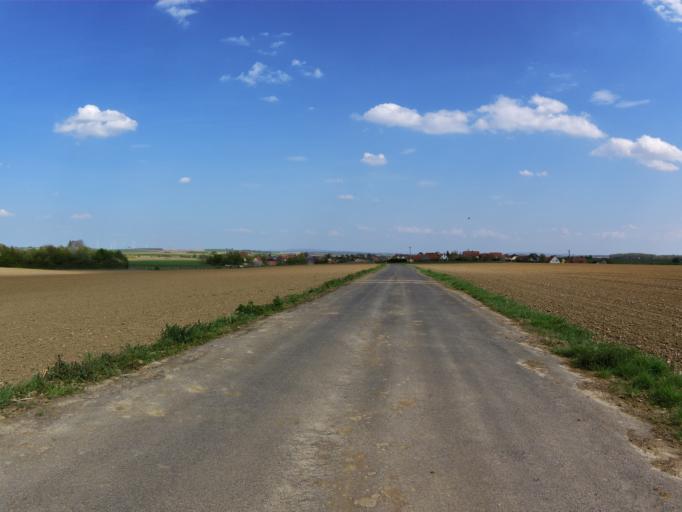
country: DE
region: Bavaria
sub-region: Regierungsbezirk Unterfranken
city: Giebelstadt
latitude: 49.6710
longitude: 9.9475
